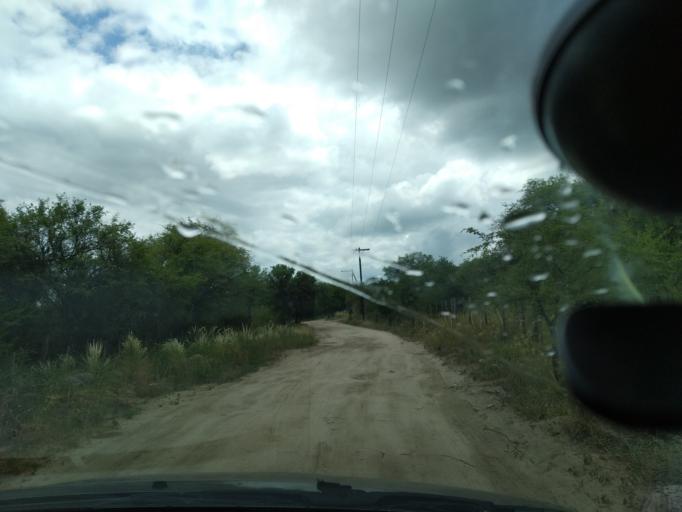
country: AR
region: Cordoba
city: Villa Las Rosas
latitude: -31.9478
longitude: -65.0368
